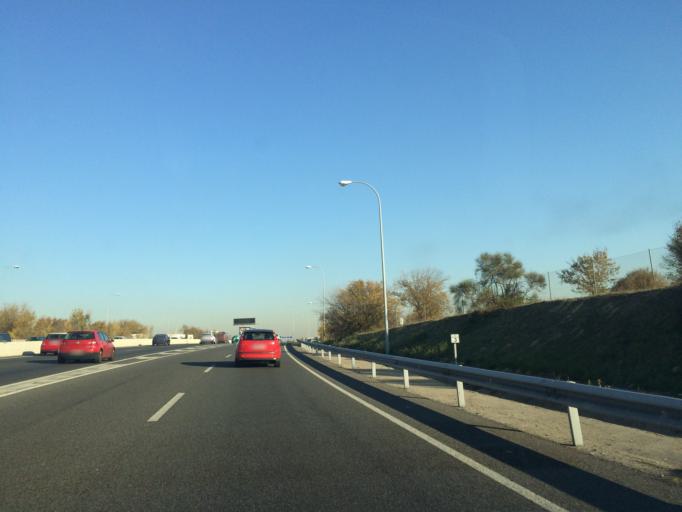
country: ES
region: Madrid
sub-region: Provincia de Madrid
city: Alcorcon
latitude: 40.3616
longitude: -3.8000
